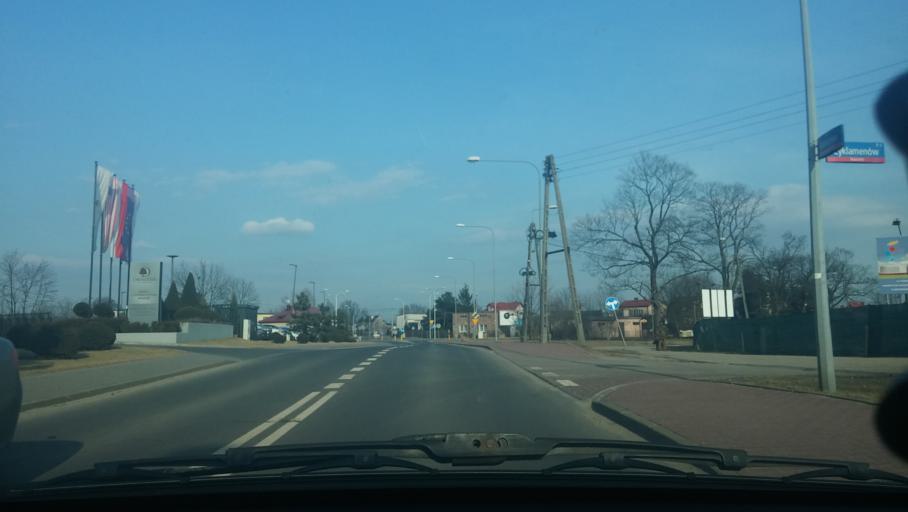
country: PL
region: Masovian Voivodeship
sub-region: Warszawa
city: Wawer
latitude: 52.1851
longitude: 21.1416
